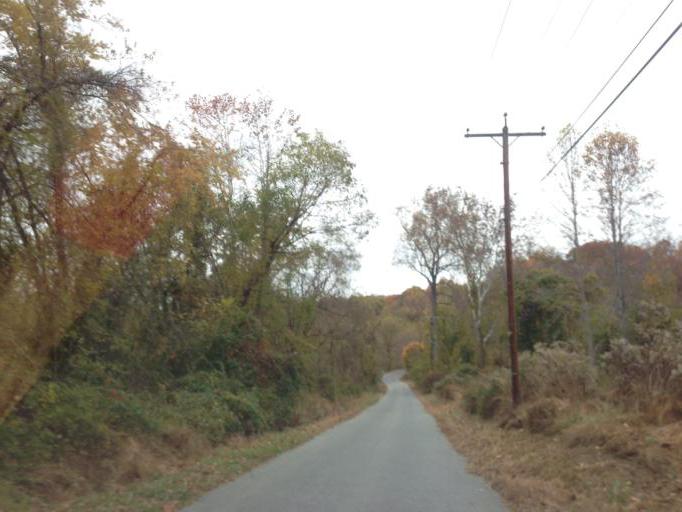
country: US
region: Maryland
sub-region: Baltimore County
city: Randallstown
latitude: 39.3796
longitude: -76.8564
